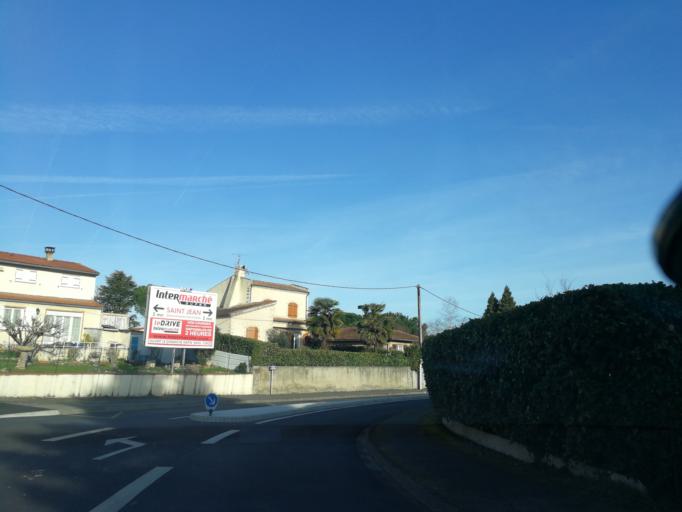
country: FR
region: Midi-Pyrenees
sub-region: Departement de la Haute-Garonne
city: Saint-Jean
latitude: 43.6534
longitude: 1.4990
